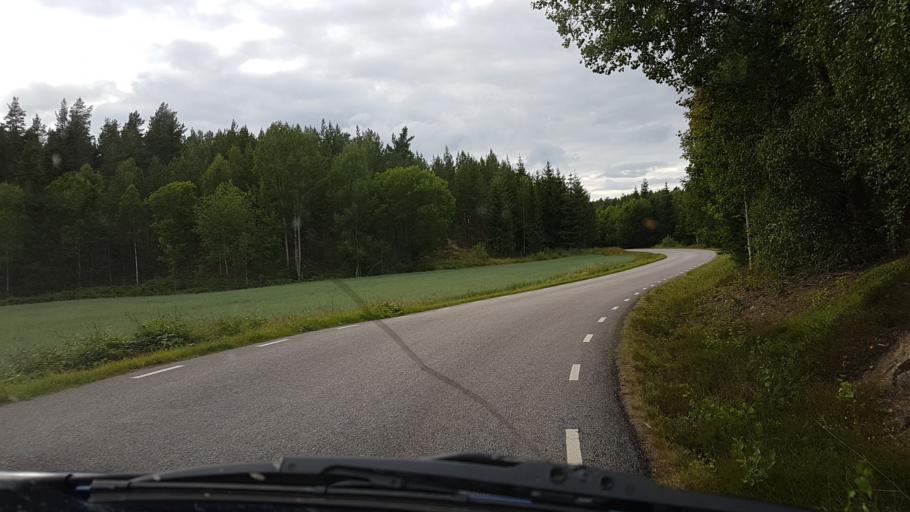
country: SE
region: OEstergoetland
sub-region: Valdemarsviks Kommun
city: Gusum
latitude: 58.4551
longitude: 16.5938
